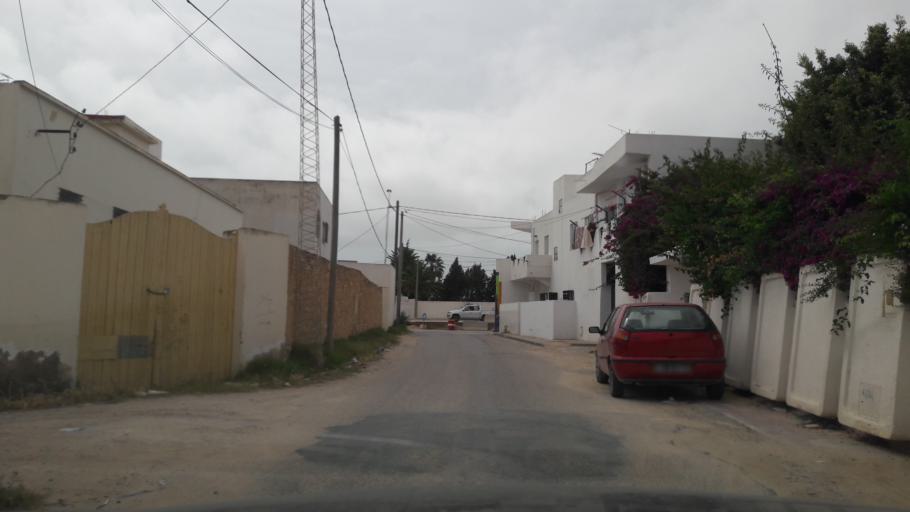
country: TN
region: Safaqis
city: Sfax
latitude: 34.7716
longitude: 10.7564
